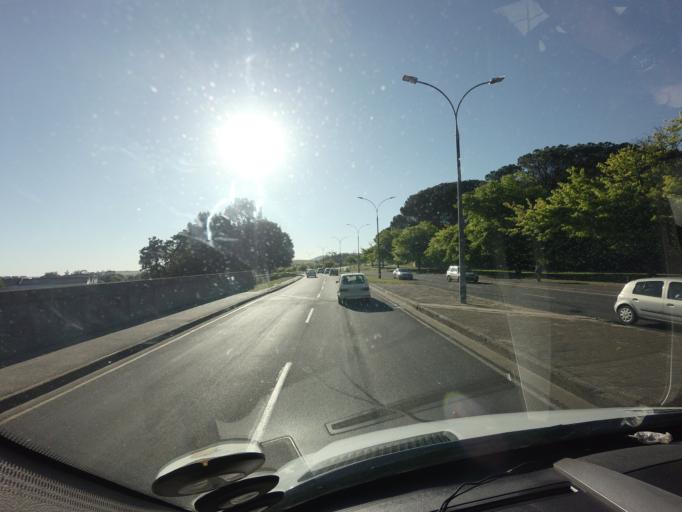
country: ZA
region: Western Cape
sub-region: Cape Winelands District Municipality
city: Stellenbosch
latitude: -33.9424
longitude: 18.8443
